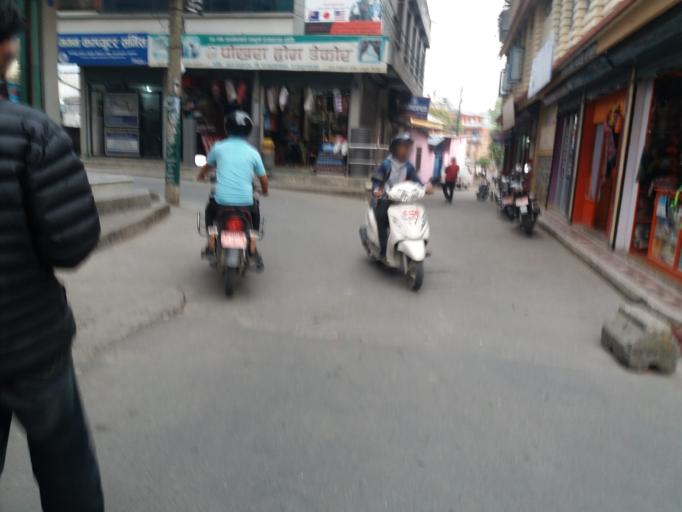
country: NP
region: Western Region
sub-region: Gandaki Zone
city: Pokhara
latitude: 28.2214
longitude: 83.9882
